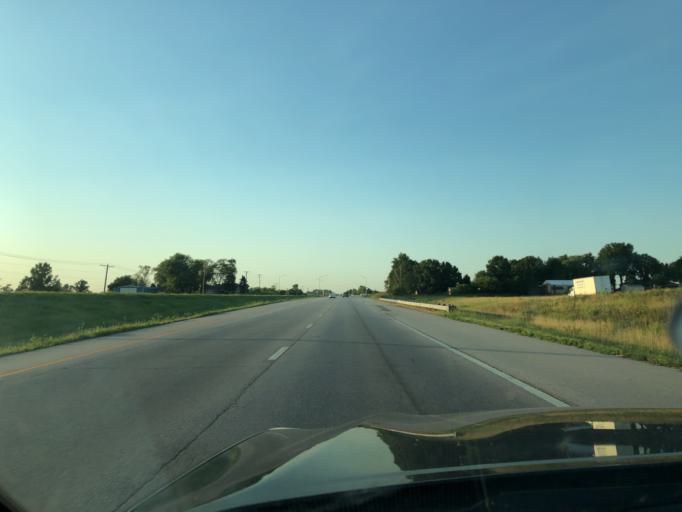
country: US
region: Kansas
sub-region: Leavenworth County
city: Basehor
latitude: 39.1545
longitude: -94.9006
